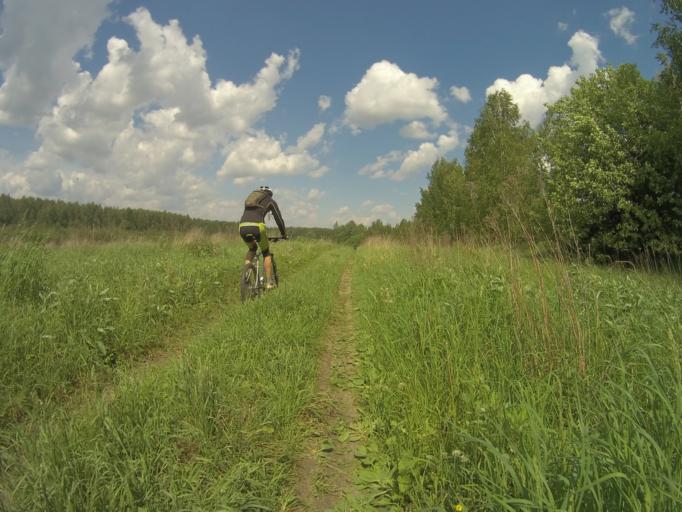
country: RU
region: Vladimir
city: Raduzhnyy
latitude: 56.0112
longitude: 40.2267
